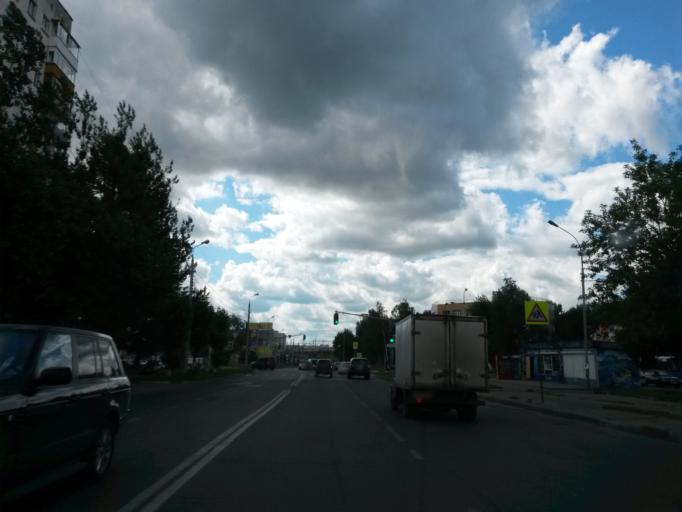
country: RU
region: Jaroslavl
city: Yaroslavl
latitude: 57.6215
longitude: 39.8485
